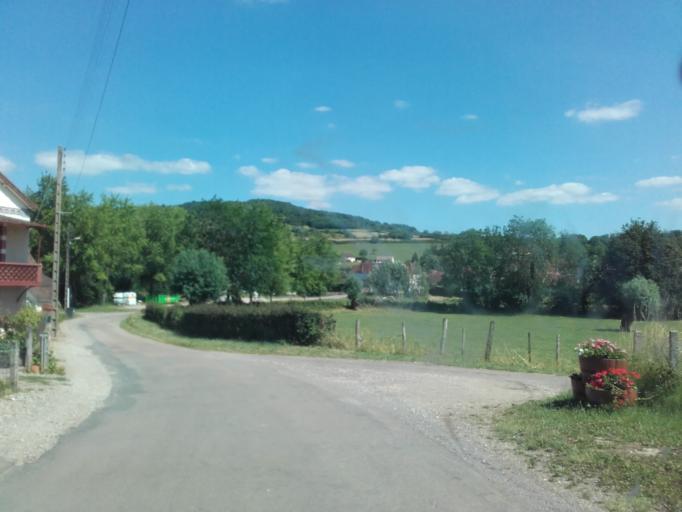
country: FR
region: Bourgogne
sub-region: Departement de Saone-et-Loire
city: Saint-Leger-sur-Dheune
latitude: 46.8805
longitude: 4.6602
